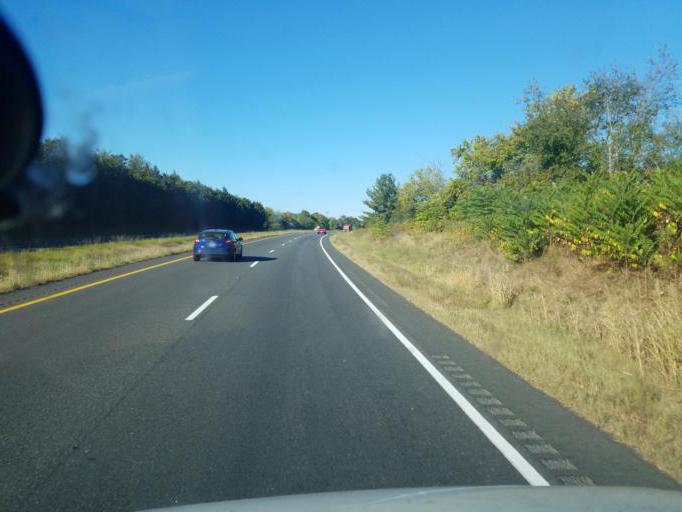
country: US
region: Virginia
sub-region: Culpeper County
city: Culpeper
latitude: 38.5040
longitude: -77.8860
